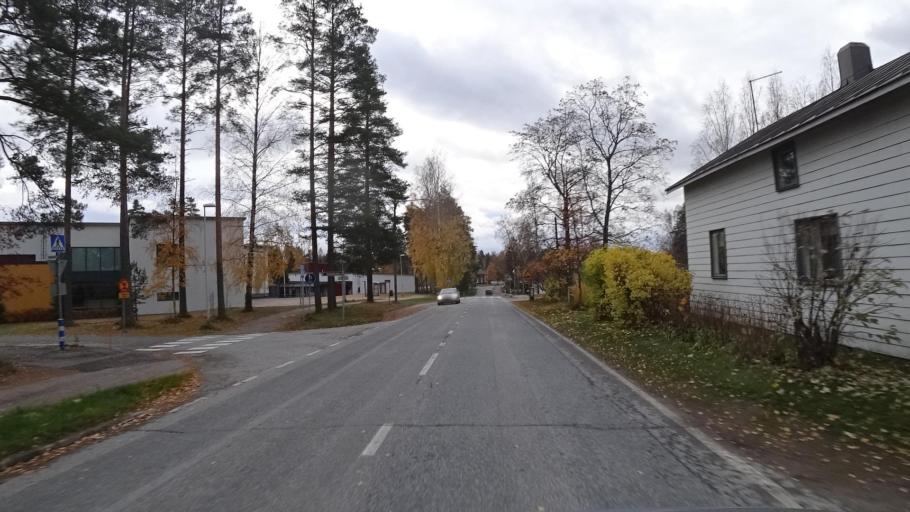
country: FI
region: Central Finland
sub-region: Joutsa
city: Joutsa
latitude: 61.7474
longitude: 26.1213
